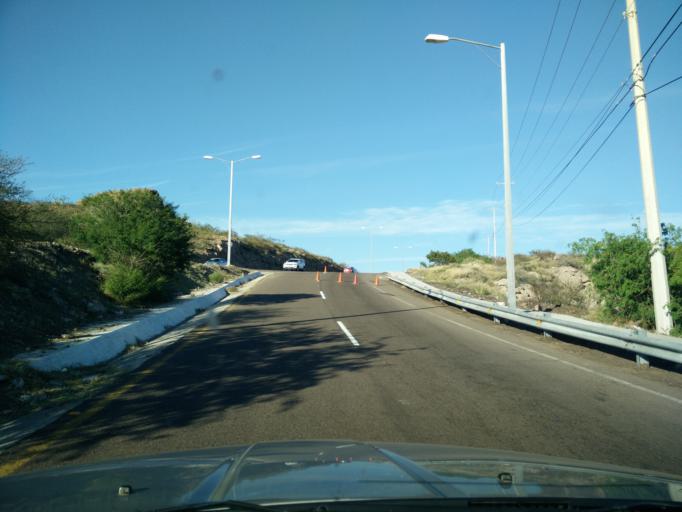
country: MX
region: Sonora
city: Heroica Guaymas
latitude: 27.9522
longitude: -111.0596
